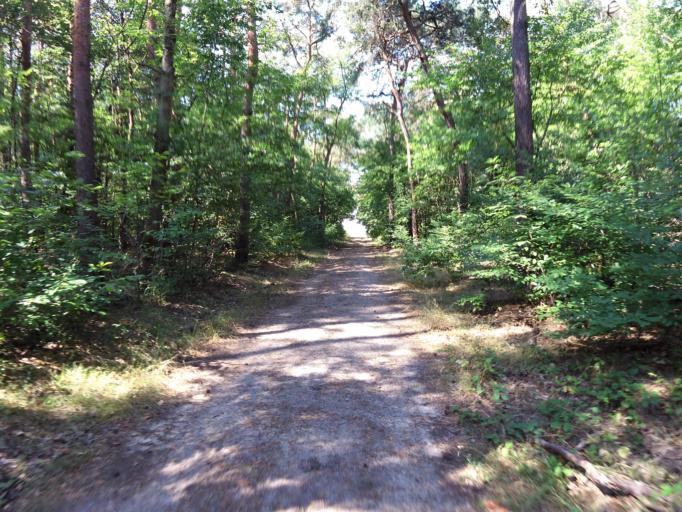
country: DE
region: Hesse
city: Lampertheim
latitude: 49.6060
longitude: 8.4967
